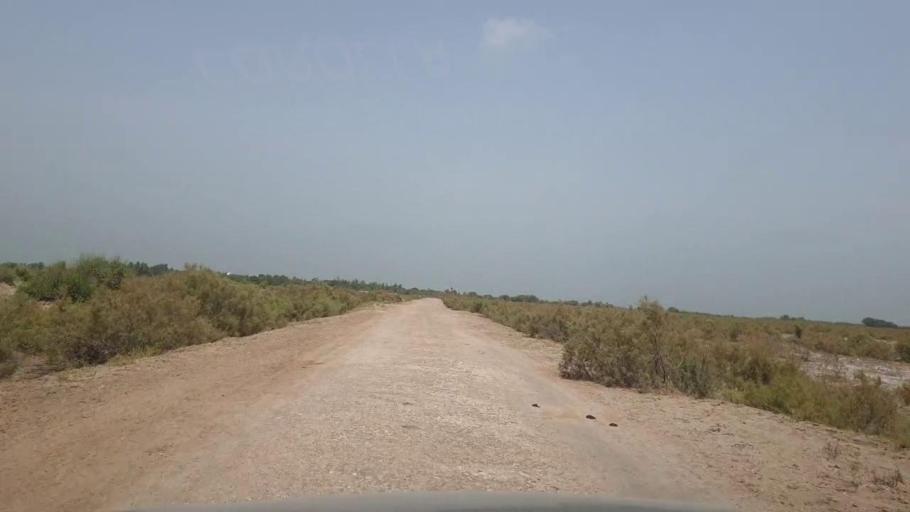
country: PK
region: Sindh
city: Garhi Yasin
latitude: 27.9150
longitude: 68.3786
